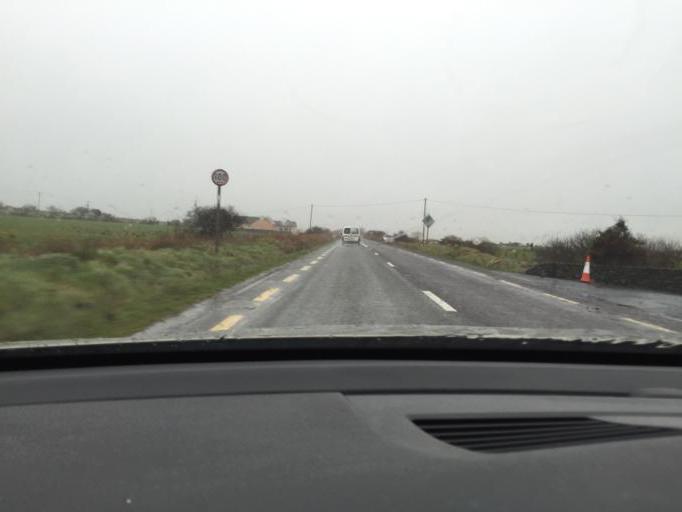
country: IE
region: Munster
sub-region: Ciarrai
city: Dingle
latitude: 52.1404
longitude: -10.2117
